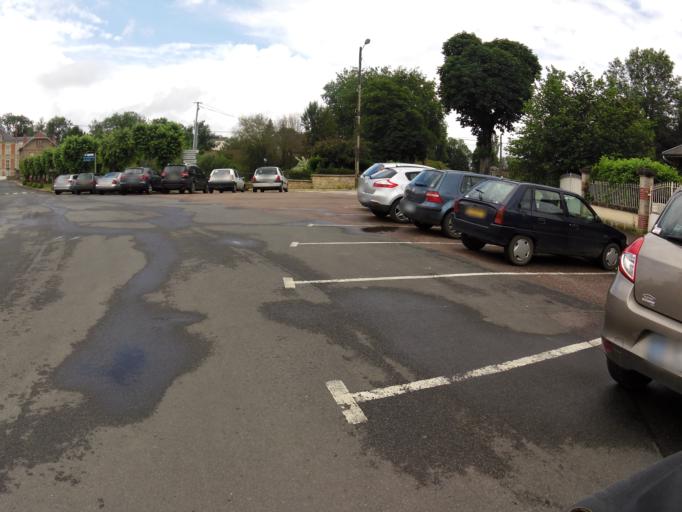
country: FR
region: Champagne-Ardenne
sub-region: Departement de la Marne
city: Sermaize-les-Bains
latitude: 48.7858
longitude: 4.9104
